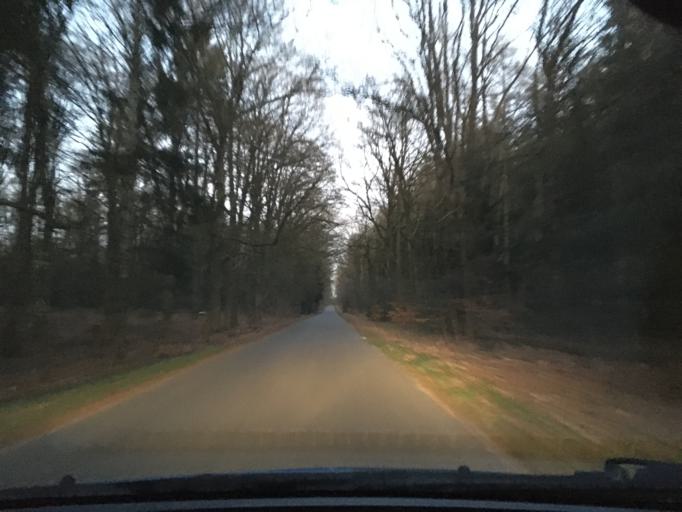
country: DE
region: Lower Saxony
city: Rehlingen
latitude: 53.0646
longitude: 10.2405
